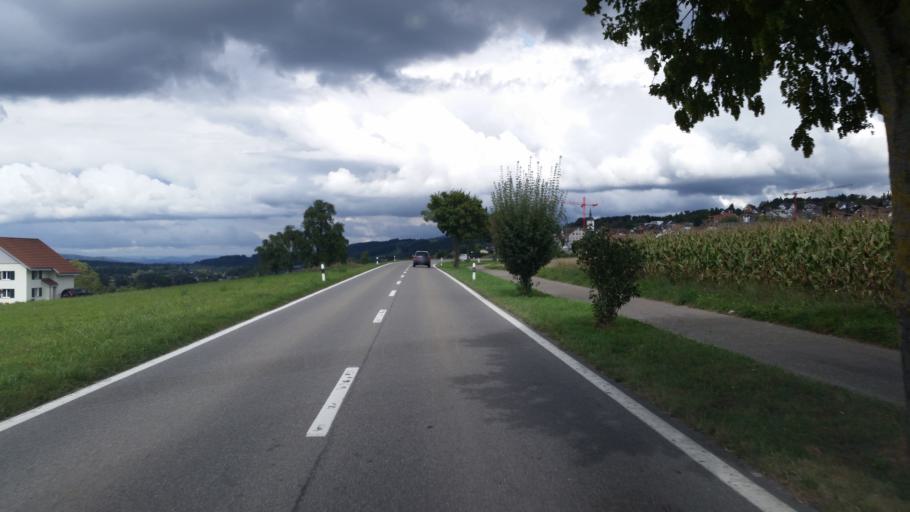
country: CH
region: Aargau
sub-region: Bezirk Bremgarten
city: Oberlunkhofen
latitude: 47.3053
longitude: 8.3908
